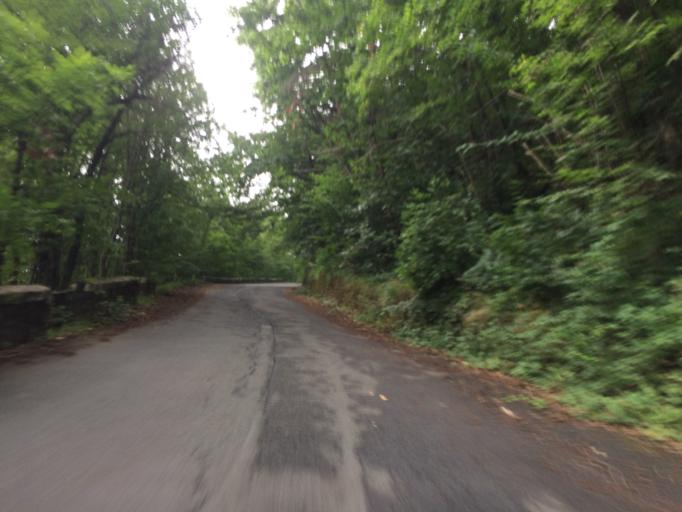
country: IT
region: Liguria
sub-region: Provincia di Imperia
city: Triora
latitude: 43.9845
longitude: 7.7578
